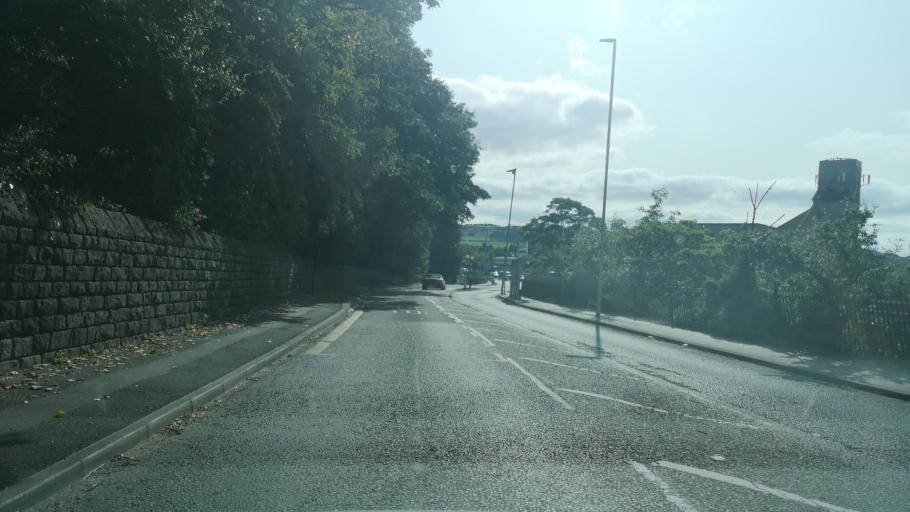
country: GB
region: England
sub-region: Kirklees
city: Dewsbury
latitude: 53.6795
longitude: -1.6359
